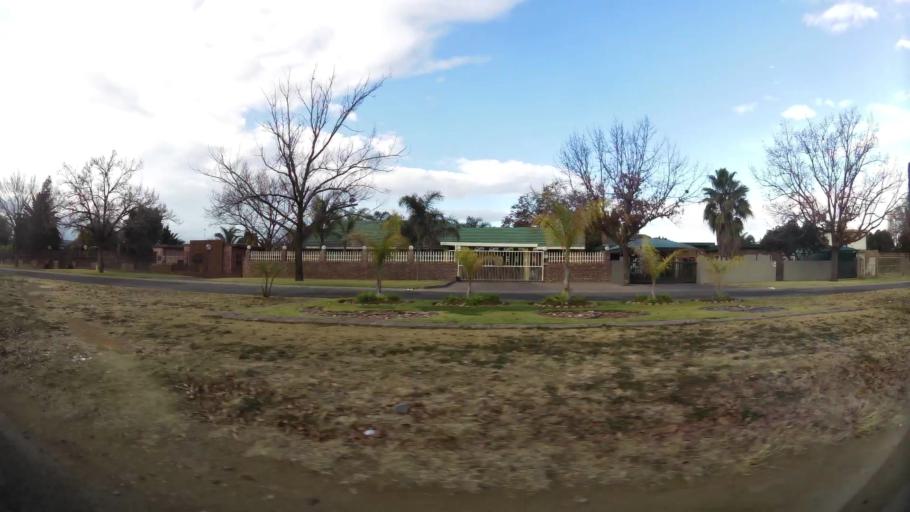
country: ZA
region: Orange Free State
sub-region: Lejweleputswa District Municipality
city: Welkom
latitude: -27.9953
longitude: 26.7330
